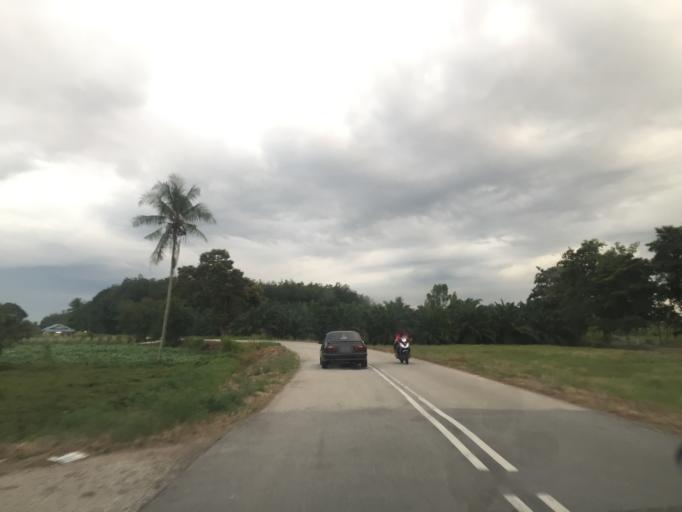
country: MY
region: Penang
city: Tasek Glugor
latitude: 5.5365
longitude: 100.5124
